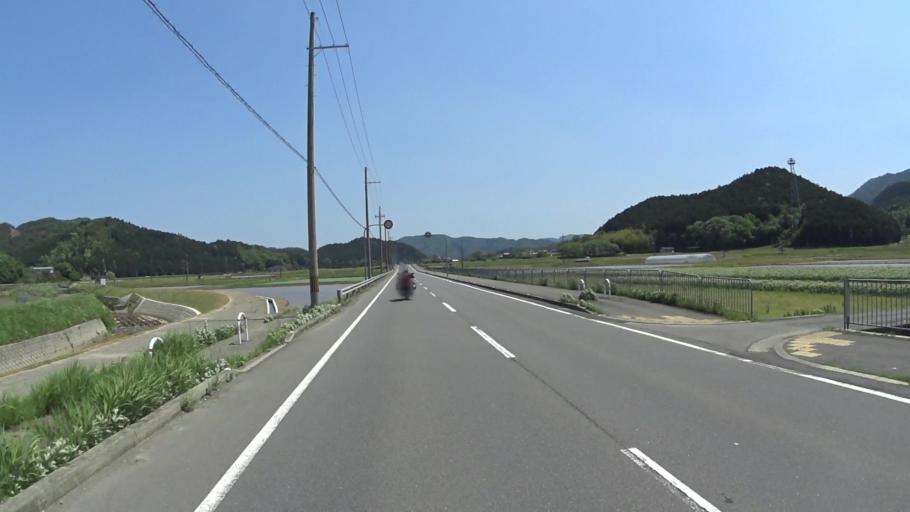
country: JP
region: Kyoto
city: Kameoka
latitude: 35.0478
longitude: 135.4777
